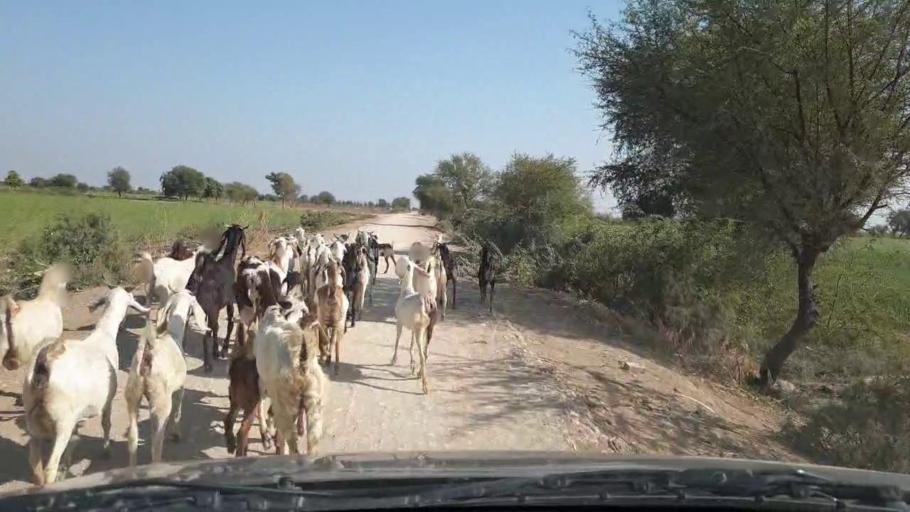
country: PK
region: Sindh
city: Samaro
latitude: 25.1981
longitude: 69.2702
